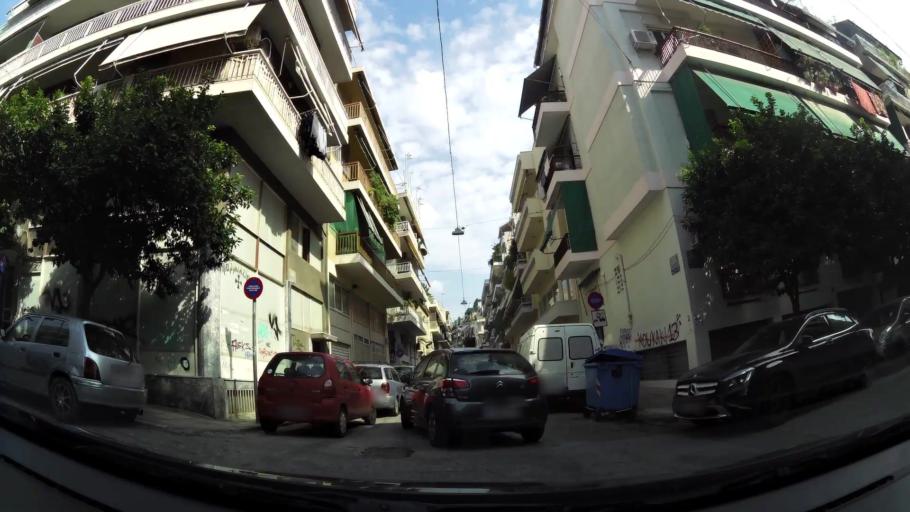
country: GR
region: Attica
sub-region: Nomarchia Athinas
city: Athens
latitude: 37.9647
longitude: 23.7224
